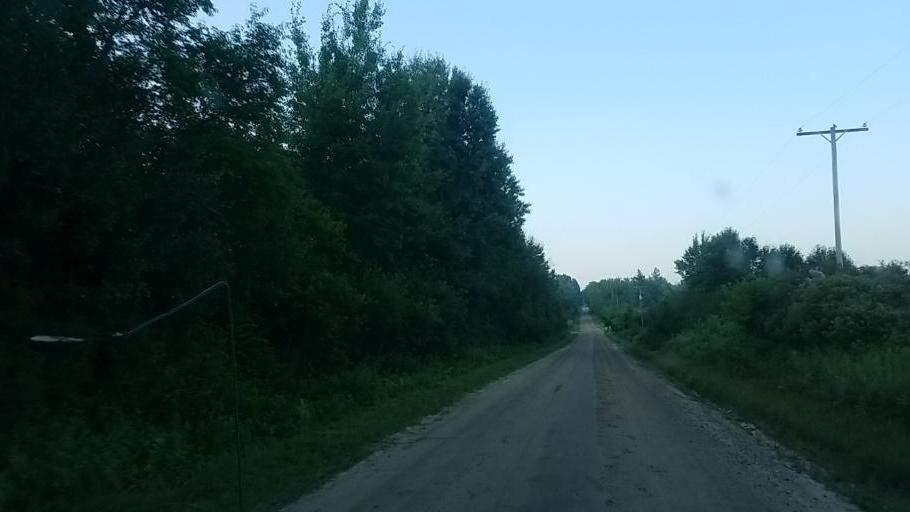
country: US
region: Michigan
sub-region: Osceola County
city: Evart
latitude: 43.9093
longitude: -85.1679
